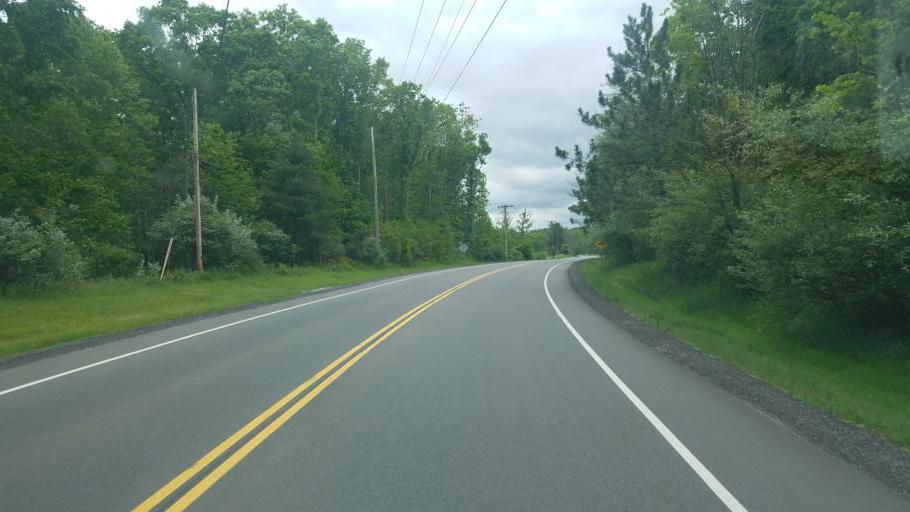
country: US
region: Ohio
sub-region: Summit County
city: Peninsula
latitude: 41.2382
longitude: -81.5360
